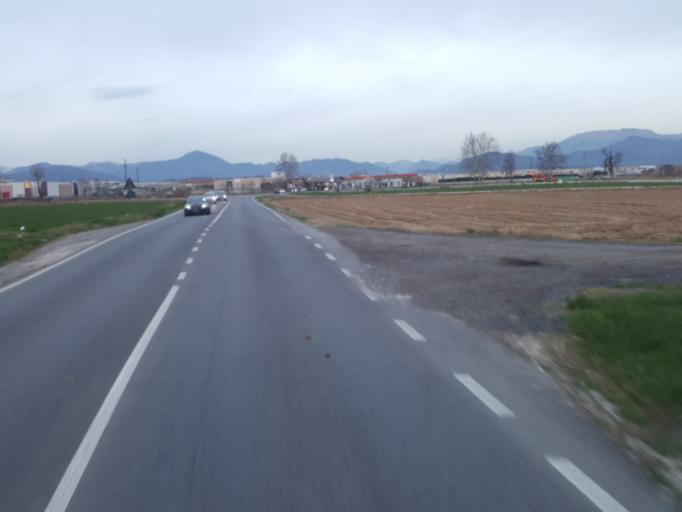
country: IT
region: Lombardy
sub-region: Provincia di Brescia
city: Rovato
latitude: 45.5523
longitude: 10.0114
